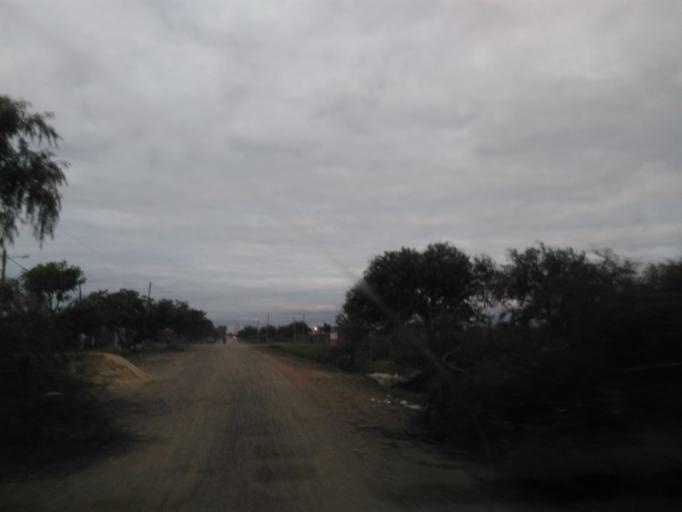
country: AR
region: Chaco
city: Resistencia
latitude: -27.4798
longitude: -59.0097
